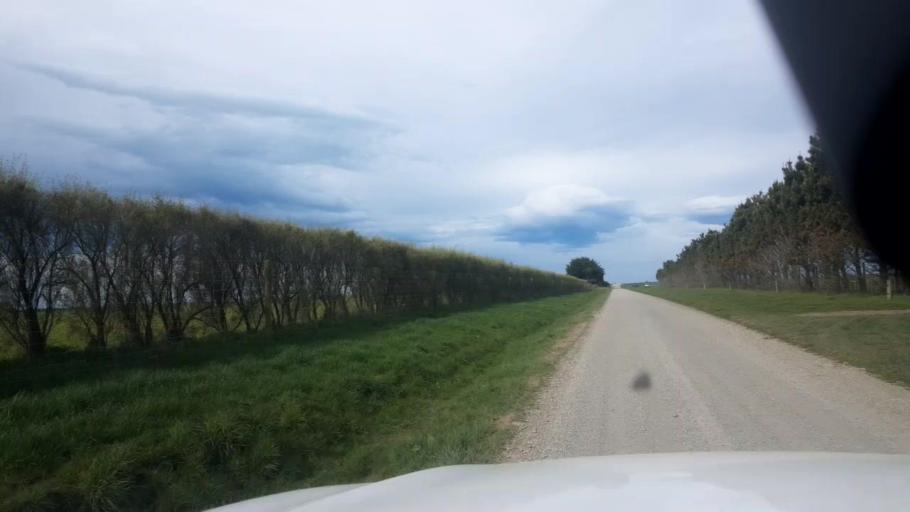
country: NZ
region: Canterbury
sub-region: Timaru District
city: Timaru
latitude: -44.2887
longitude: 171.3326
